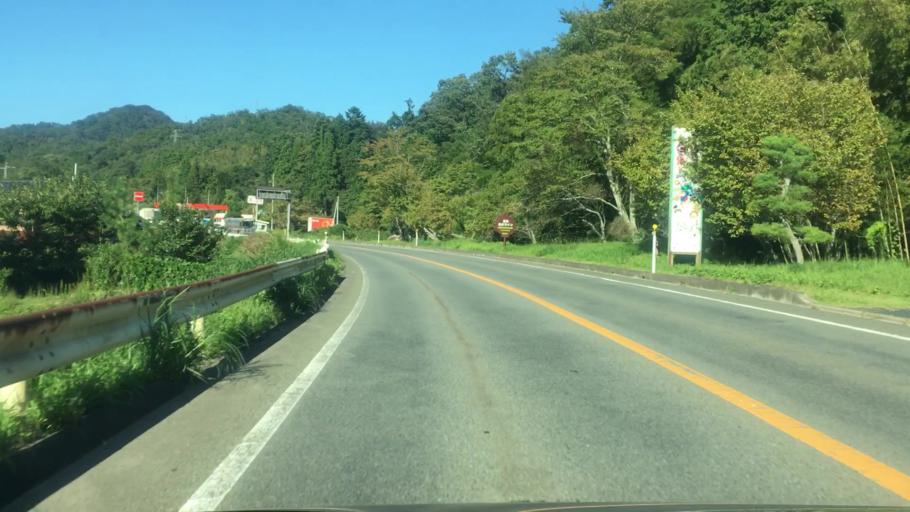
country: JP
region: Hyogo
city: Toyooka
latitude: 35.5586
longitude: 134.8503
